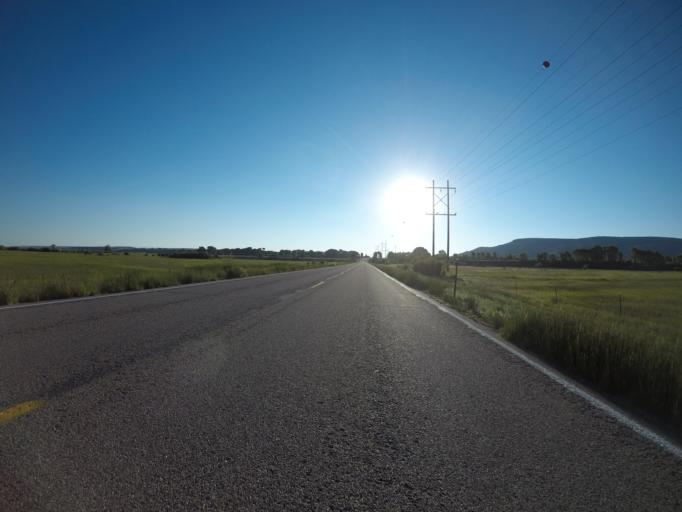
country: US
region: Wyoming
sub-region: Sublette County
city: Marbleton
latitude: 42.5737
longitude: -109.9402
